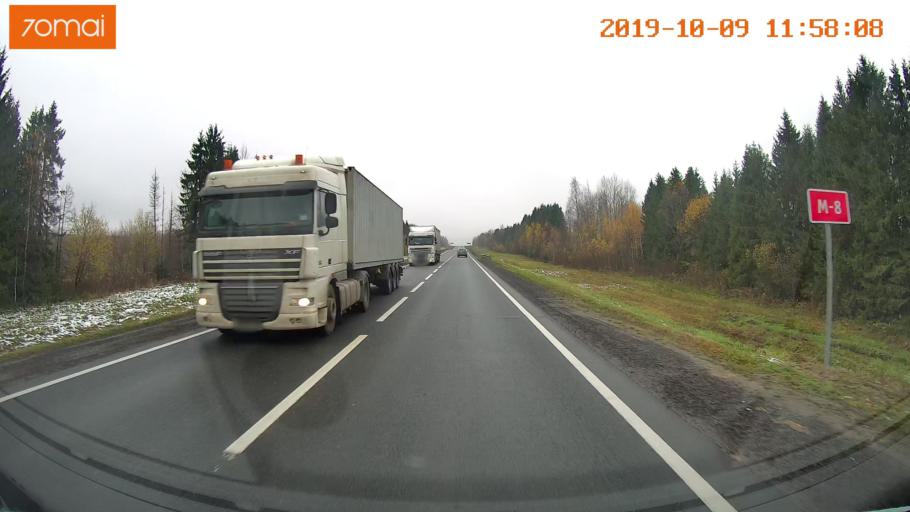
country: RU
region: Vologda
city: Gryazovets
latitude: 58.7224
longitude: 40.2961
